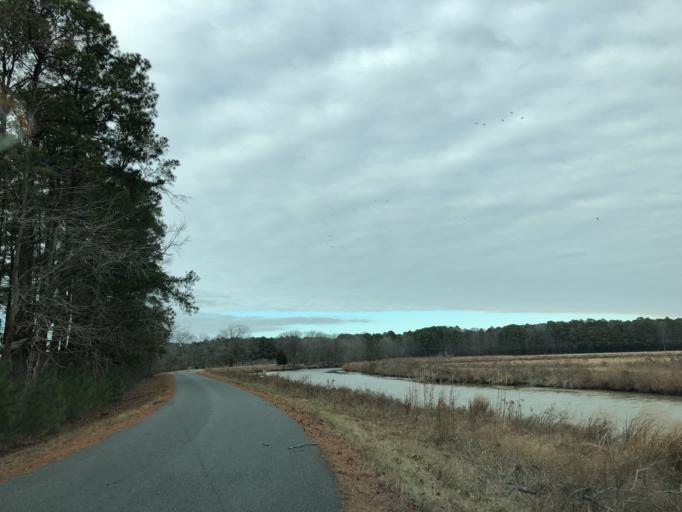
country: US
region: Maryland
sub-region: Dorchester County
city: Cambridge
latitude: 38.4419
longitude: -76.1227
